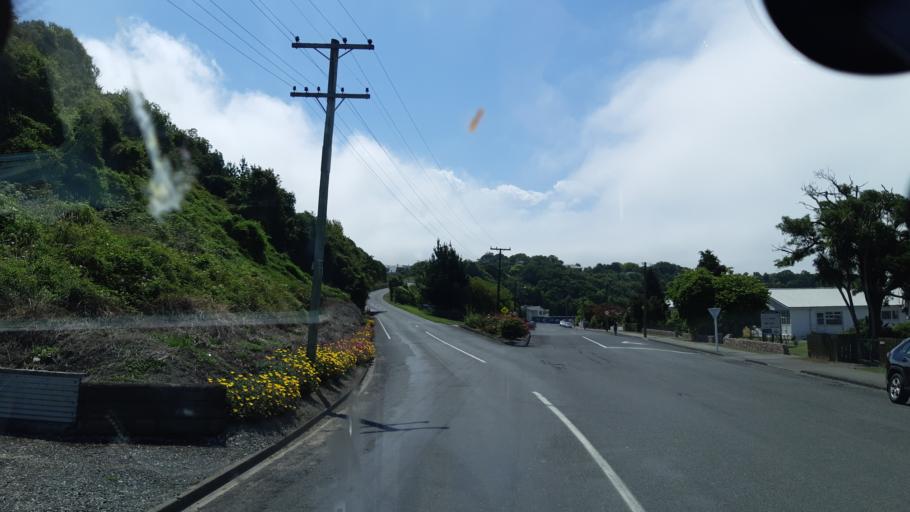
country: NZ
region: Canterbury
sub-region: Kaikoura District
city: Kaikoura
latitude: -42.4095
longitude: 173.6839
